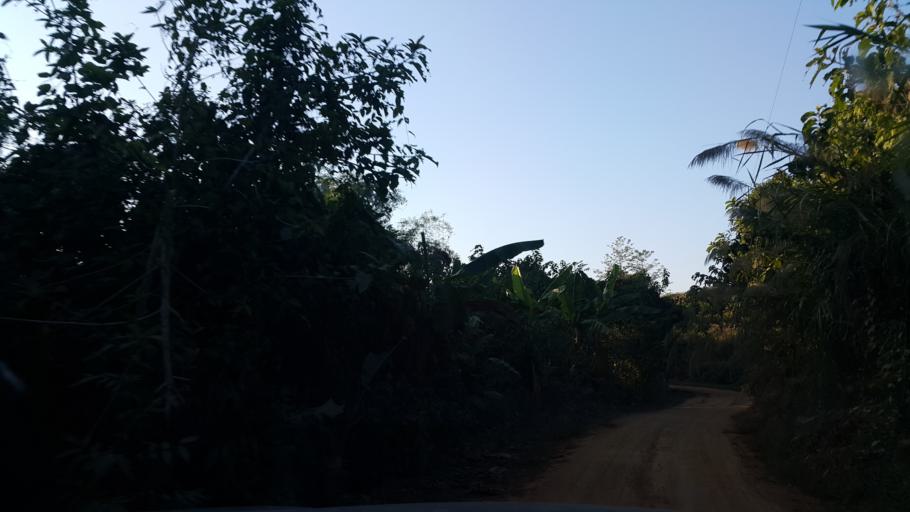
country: TH
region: Sukhothai
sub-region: Amphoe Si Satchanalai
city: Si Satchanalai
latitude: 17.5937
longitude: 99.6160
